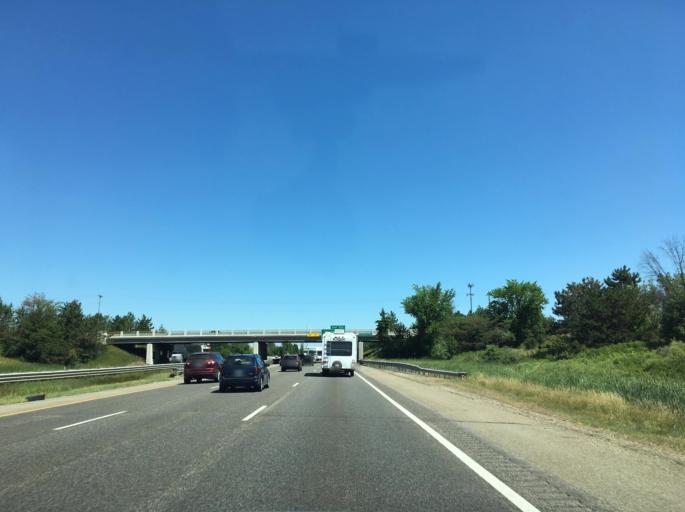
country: US
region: Michigan
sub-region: Genesee County
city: Beecher
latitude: 43.0885
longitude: -83.7628
